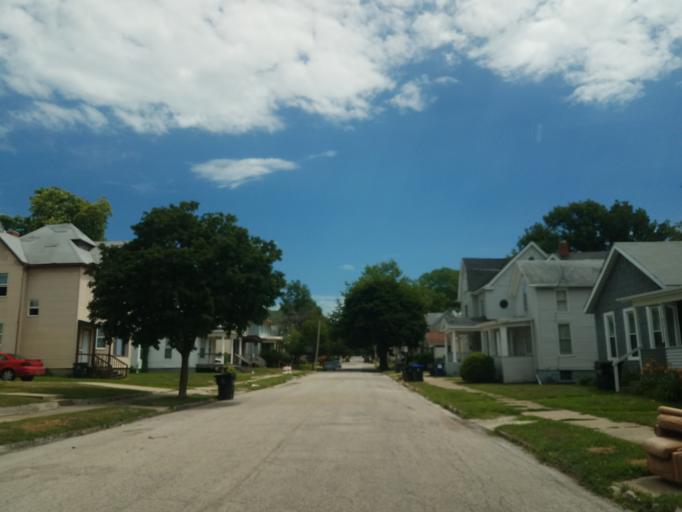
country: US
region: Illinois
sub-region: McLean County
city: Bloomington
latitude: 40.4836
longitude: -88.9904
